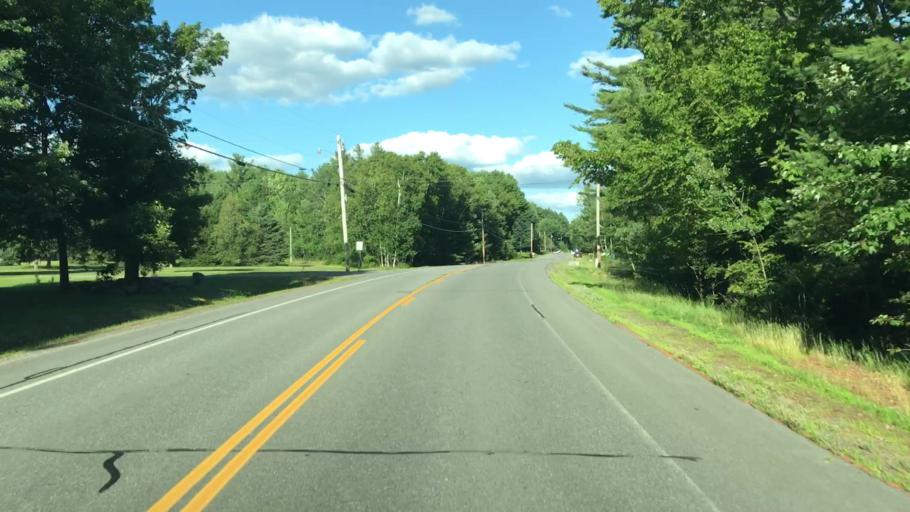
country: US
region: Maine
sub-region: Penobscot County
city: Lincoln
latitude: 45.3750
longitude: -68.4851
